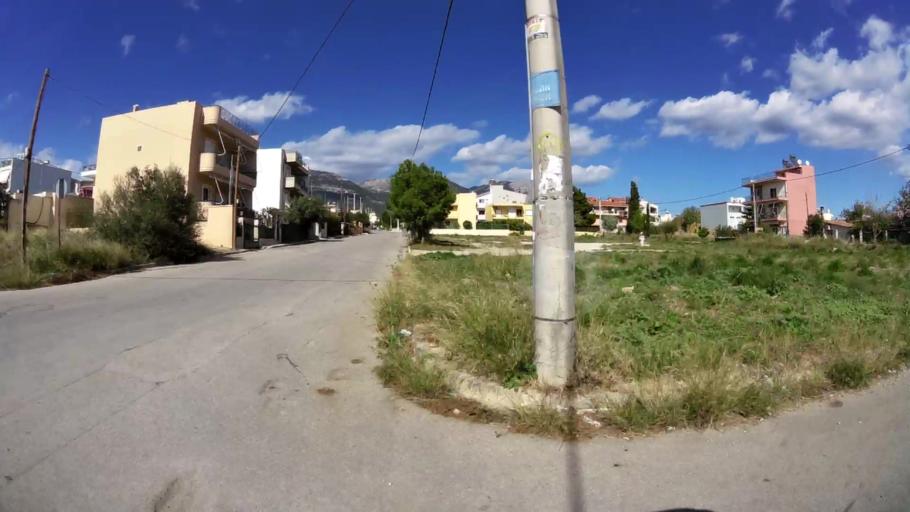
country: GR
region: Attica
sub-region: Nomarchia Anatolikis Attikis
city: Acharnes
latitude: 38.1048
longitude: 23.7396
